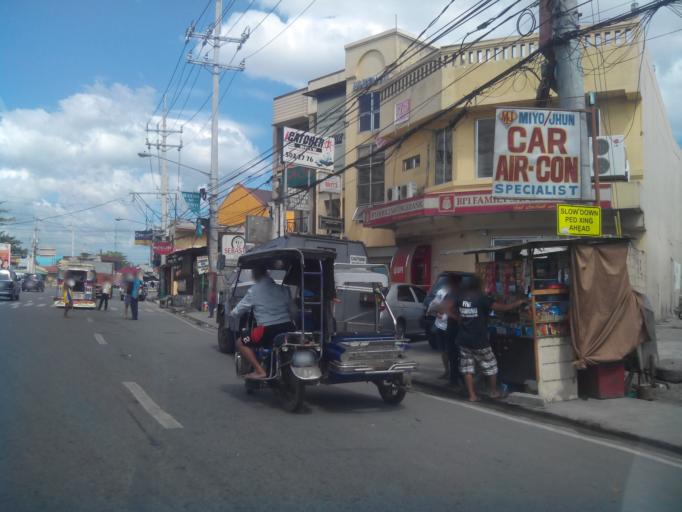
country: PH
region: Calabarzon
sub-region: Province of Rizal
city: Taytay
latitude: 14.5589
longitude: 121.1362
